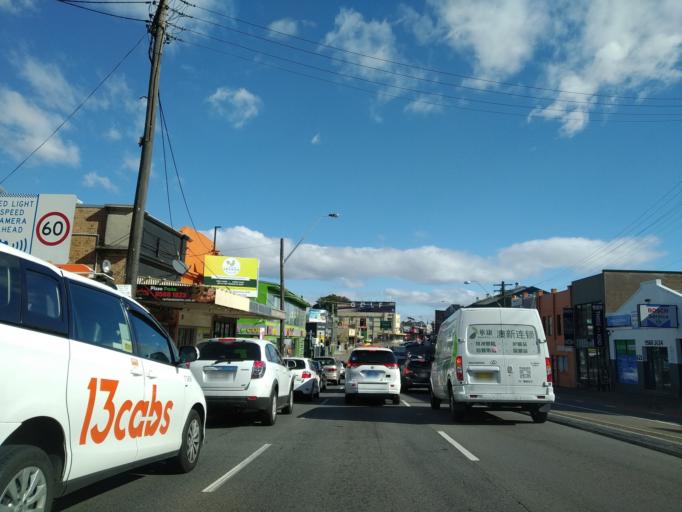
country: AU
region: New South Wales
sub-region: Marrickville
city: Lewisham
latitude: -33.8897
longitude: 151.1499
